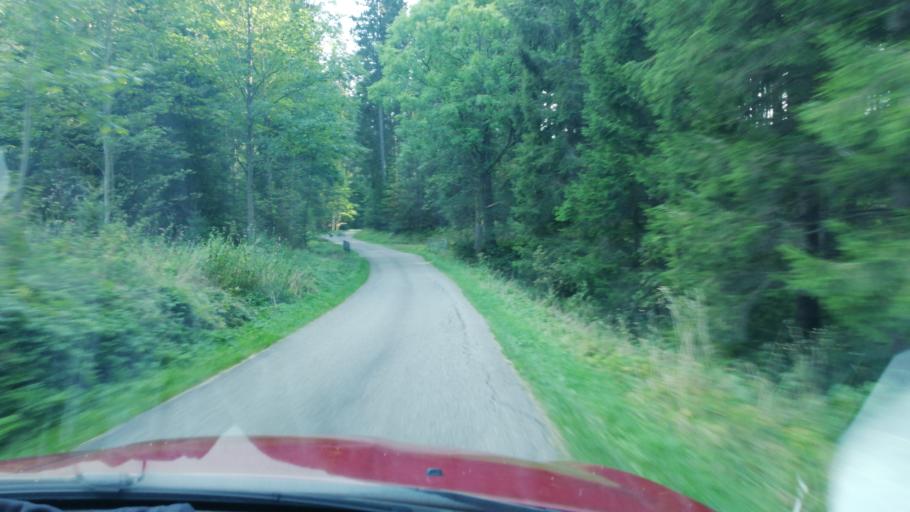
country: AT
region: Lower Austria
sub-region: Politischer Bezirk Zwettl
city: Langschlag
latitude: 48.4784
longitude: 14.8403
